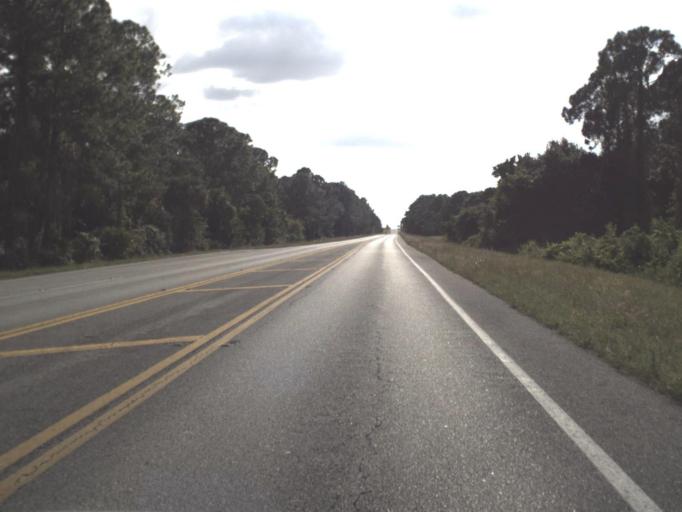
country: US
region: Florida
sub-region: Brevard County
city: Port Saint John
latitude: 28.5156
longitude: -80.8292
